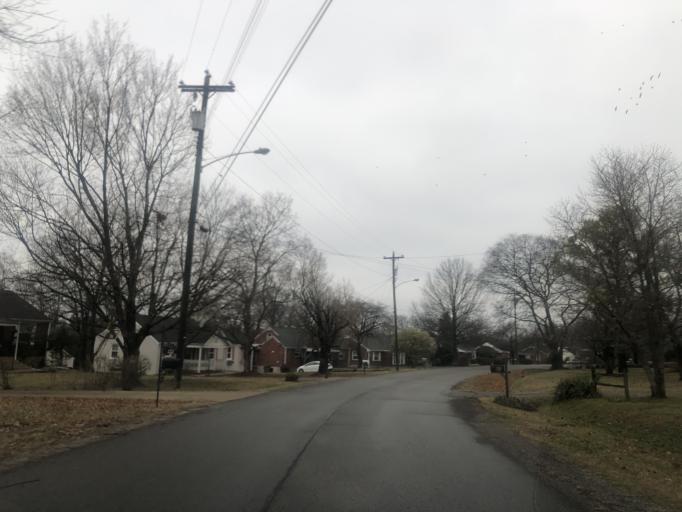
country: US
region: Tennessee
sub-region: Davidson County
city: Lakewood
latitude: 36.1648
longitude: -86.6860
